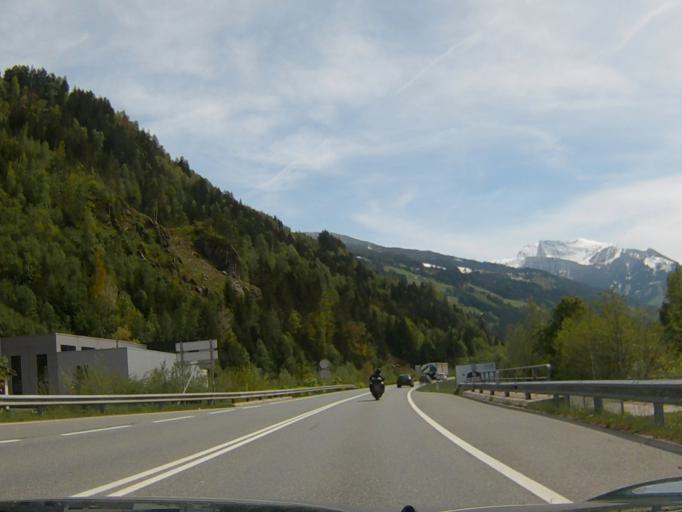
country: AT
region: Tyrol
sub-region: Politischer Bezirk Schwaz
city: Stumm
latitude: 47.2717
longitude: 11.8998
